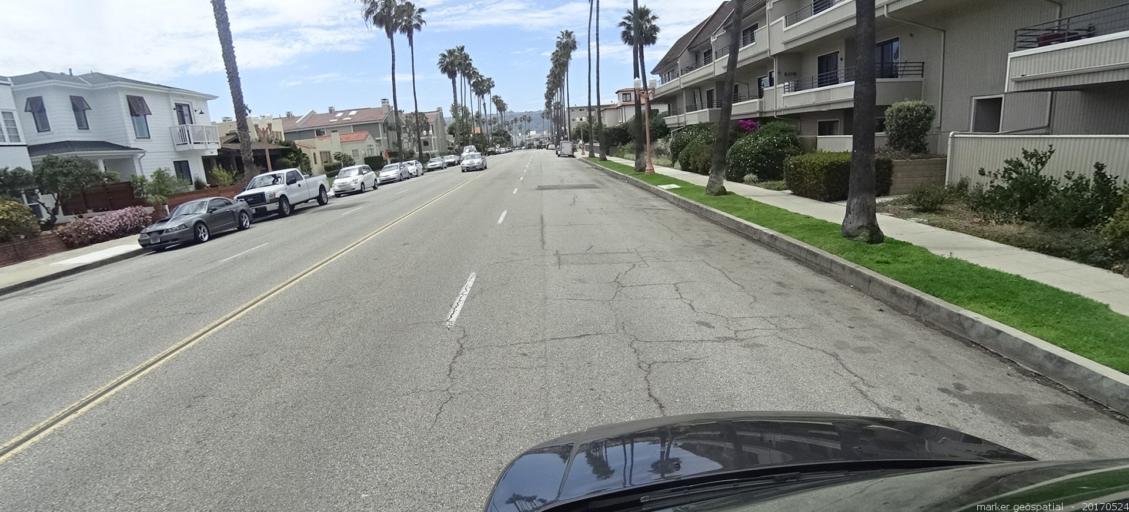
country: US
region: California
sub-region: Los Angeles County
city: Redondo Beach
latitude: 33.8313
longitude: -118.3888
